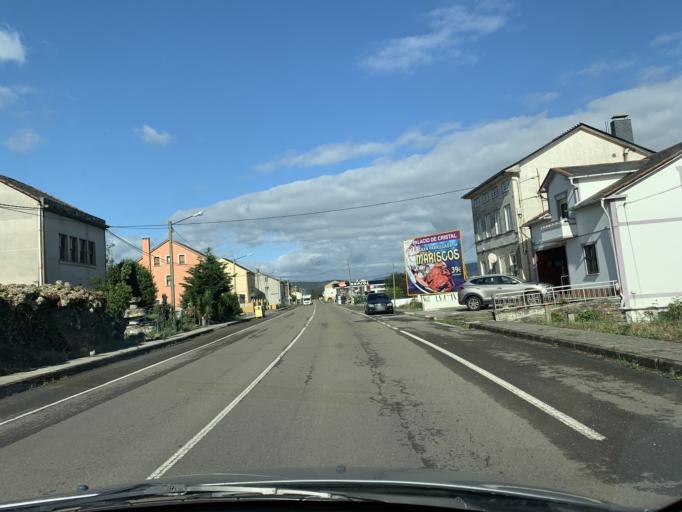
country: ES
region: Galicia
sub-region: Provincia de Lugo
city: Barreiros
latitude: 43.5399
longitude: -7.2401
